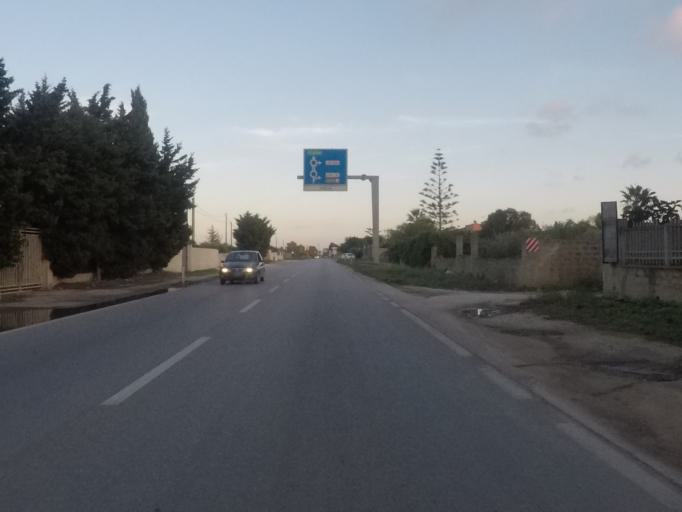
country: IT
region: Sicily
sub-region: Trapani
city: Mazara II
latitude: 37.6806
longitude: 12.5749
